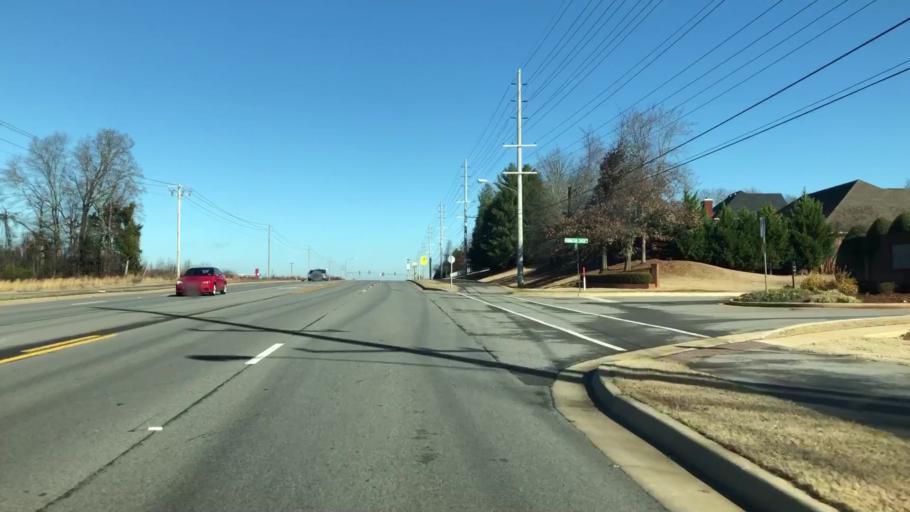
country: US
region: Alabama
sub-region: Madison County
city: Madison
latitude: 34.7026
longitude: -86.7865
